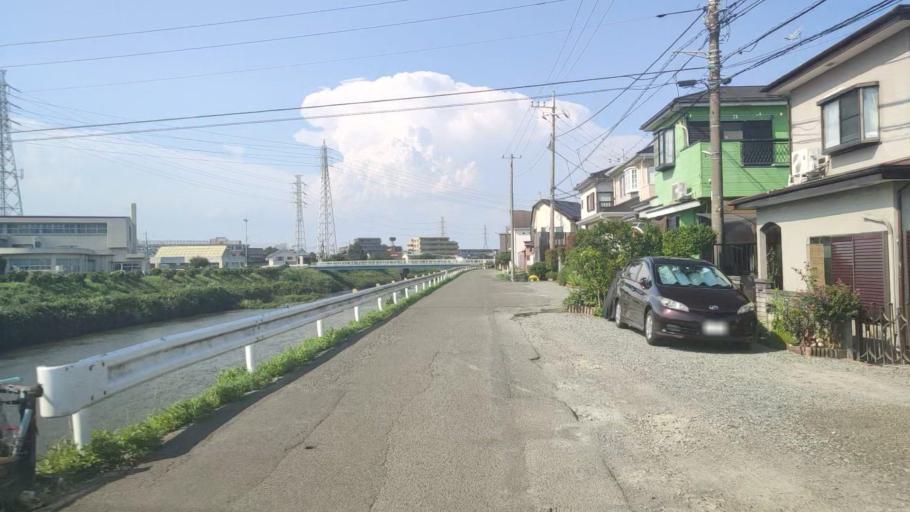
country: JP
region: Kanagawa
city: Hiratsuka
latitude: 35.3467
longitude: 139.3252
